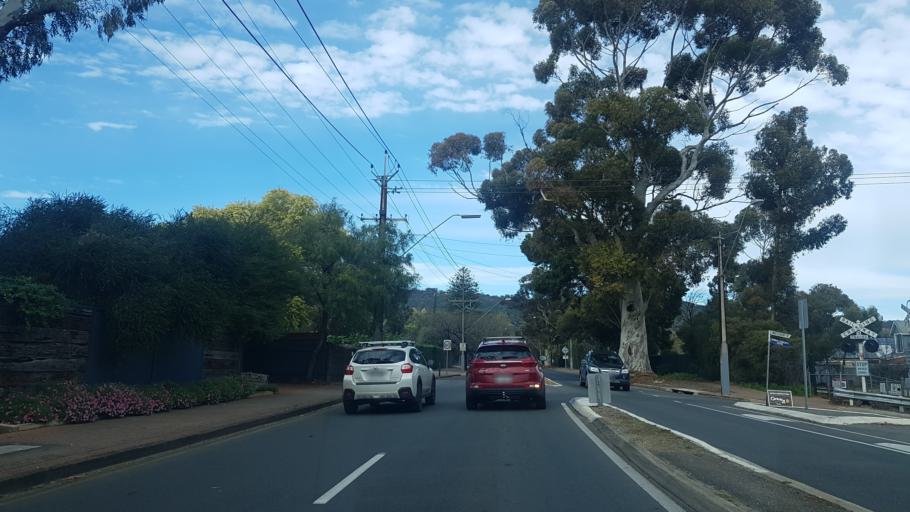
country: AU
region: South Australia
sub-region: Mitcham
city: Hawthorn
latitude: -34.9788
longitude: 138.6102
